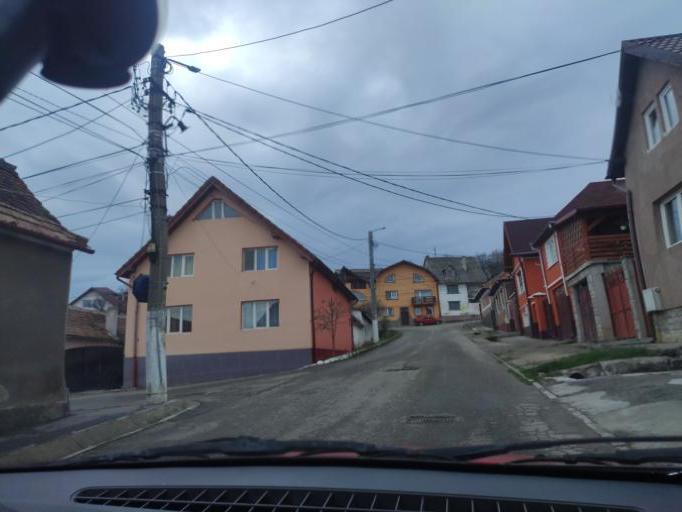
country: RO
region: Brasov
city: Codlea
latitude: 45.6964
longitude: 25.4357
